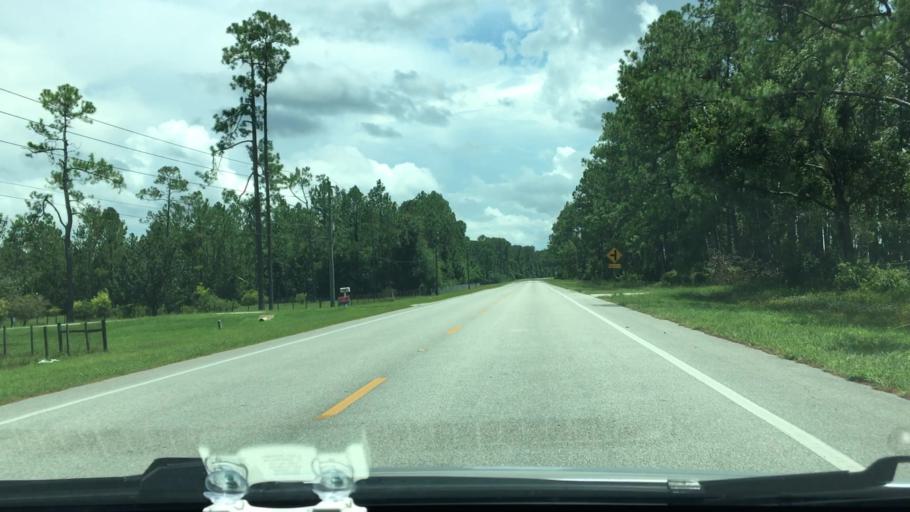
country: US
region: Florida
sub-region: Volusia County
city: Samsula-Spruce Creek
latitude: 29.0327
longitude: -81.0667
